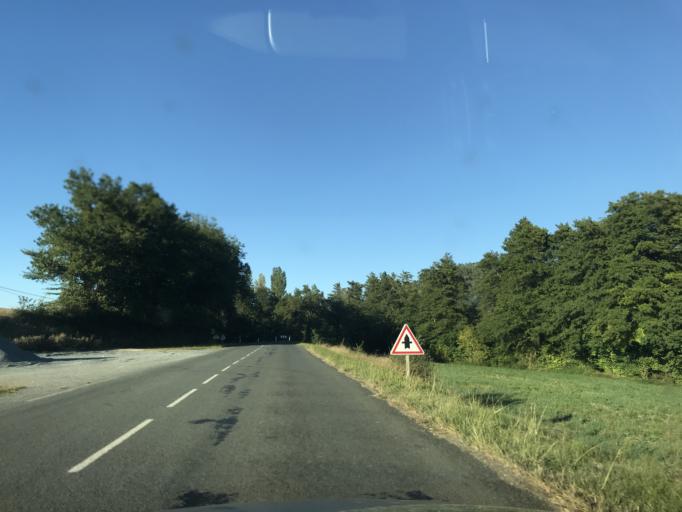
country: FR
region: Aquitaine
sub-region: Departement de la Gironde
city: Rauzan
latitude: 44.7571
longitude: -0.0682
